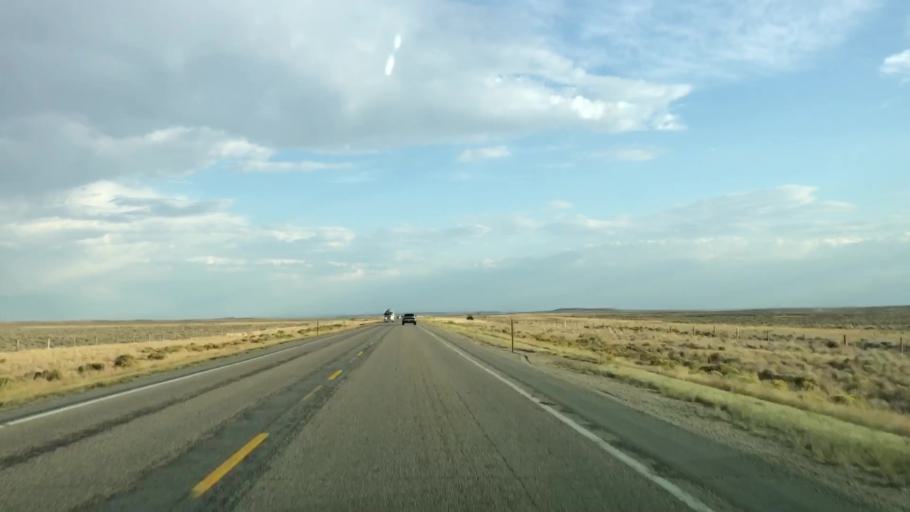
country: US
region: Wyoming
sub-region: Sublette County
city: Pinedale
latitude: 42.4038
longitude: -109.5482
